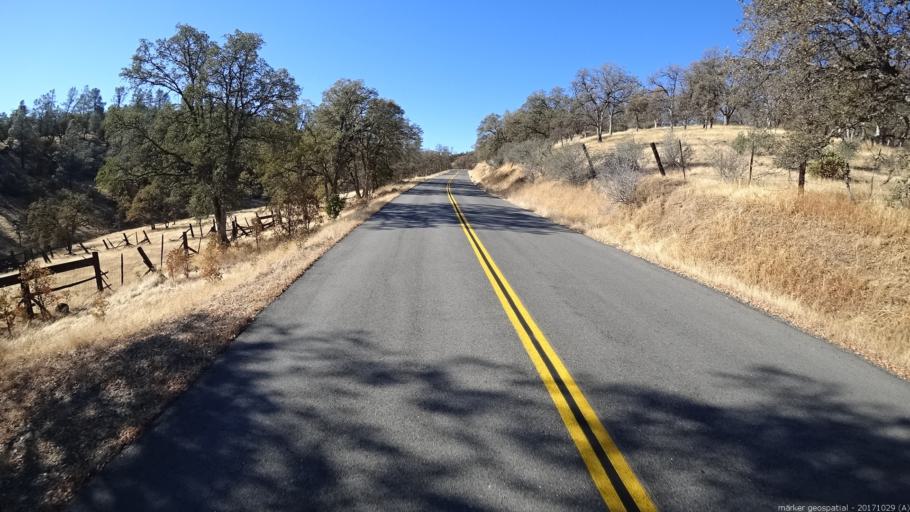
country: US
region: California
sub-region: Trinity County
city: Lewiston
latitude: 40.3896
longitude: -122.8026
